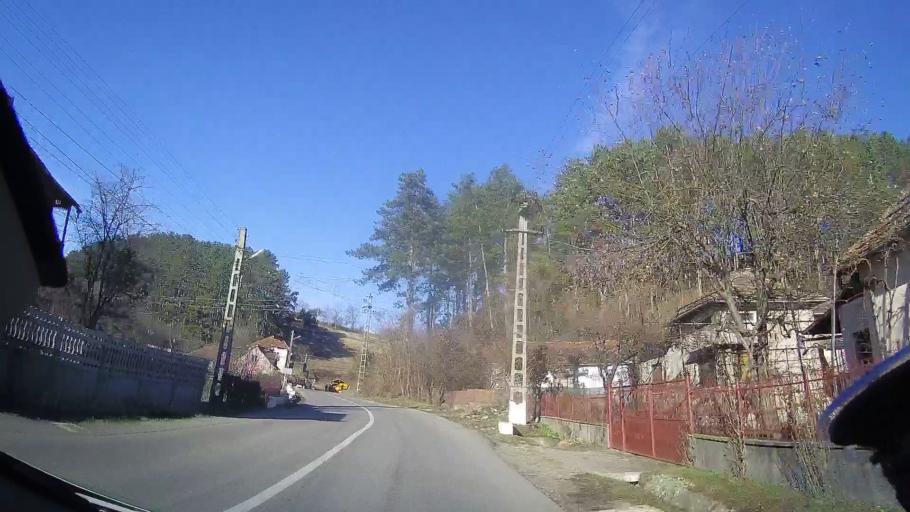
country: RO
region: Bihor
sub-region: Comuna Bratca
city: Bratca
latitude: 46.9298
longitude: 22.6016
